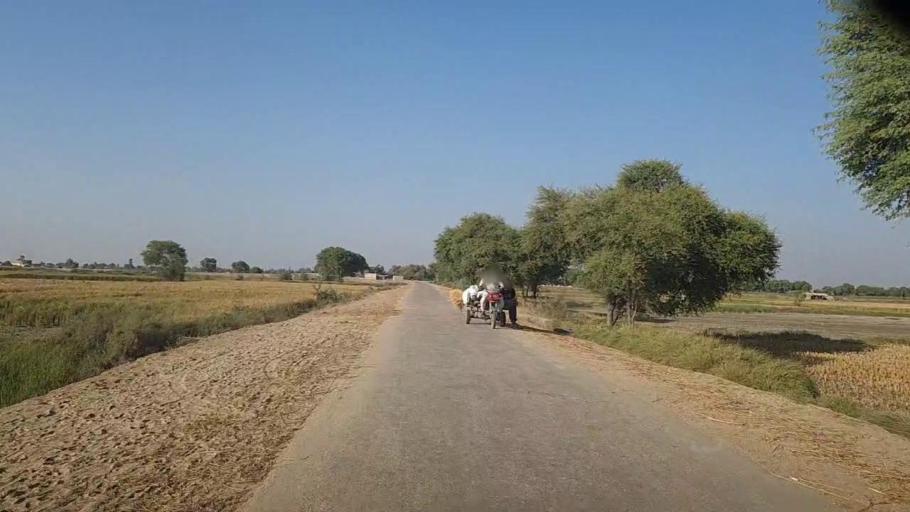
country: PK
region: Sindh
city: Tangwani
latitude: 28.2974
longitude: 68.9518
